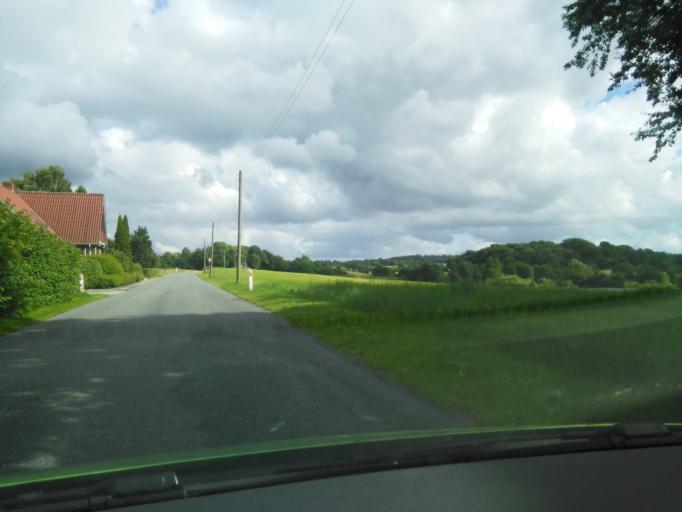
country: DK
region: Central Jutland
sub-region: Horsens Kommune
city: Braedstrup
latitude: 55.9710
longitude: 9.7075
